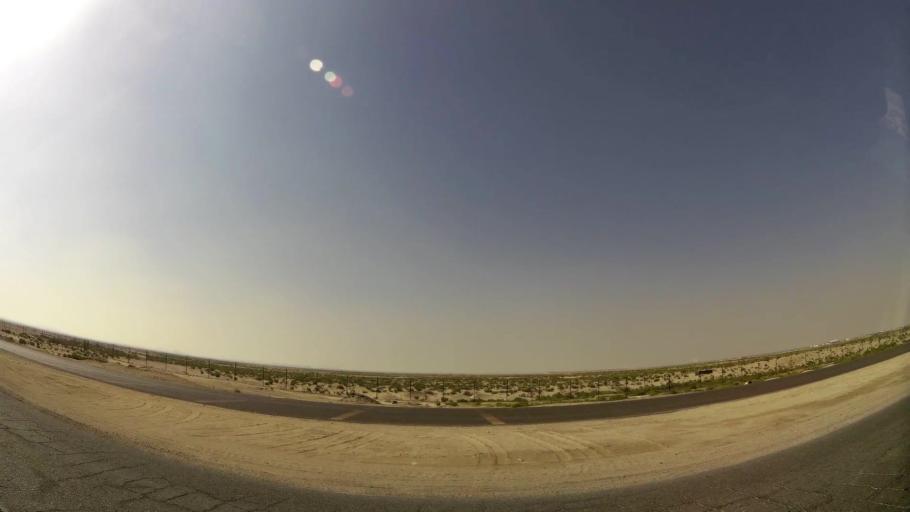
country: AE
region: Dubai
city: Dubai
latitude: 24.9587
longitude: 55.0184
